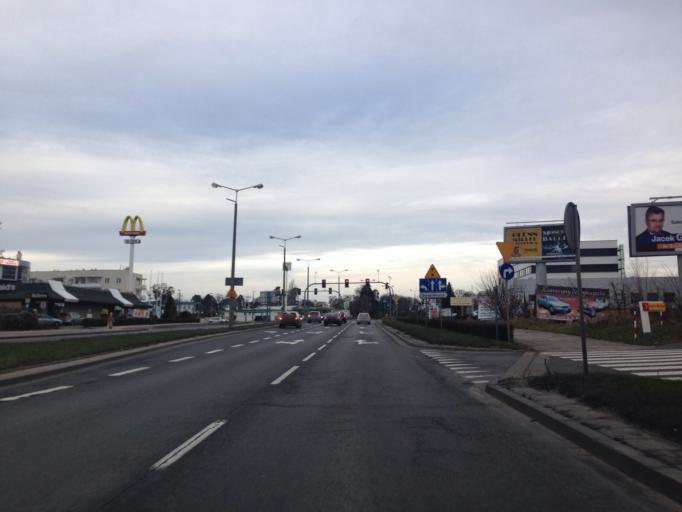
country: PL
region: Kujawsko-Pomorskie
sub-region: Torun
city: Torun
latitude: 53.0302
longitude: 18.6108
